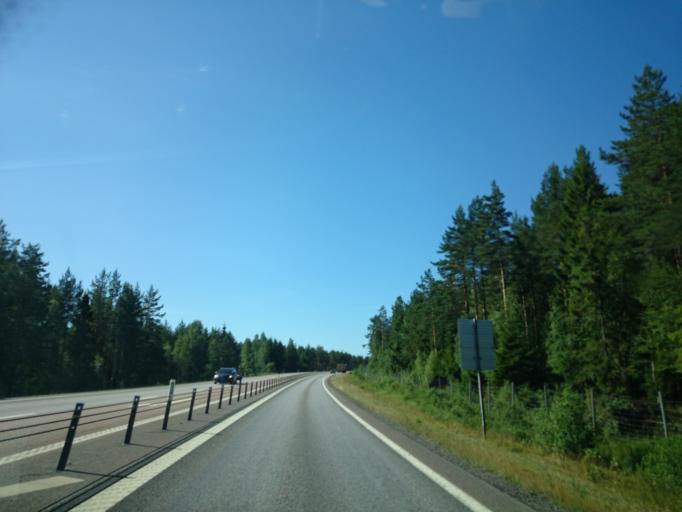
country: SE
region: Gaevleborg
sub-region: Soderhamns Kommun
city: Ljusne
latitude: 61.1730
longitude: 17.0471
